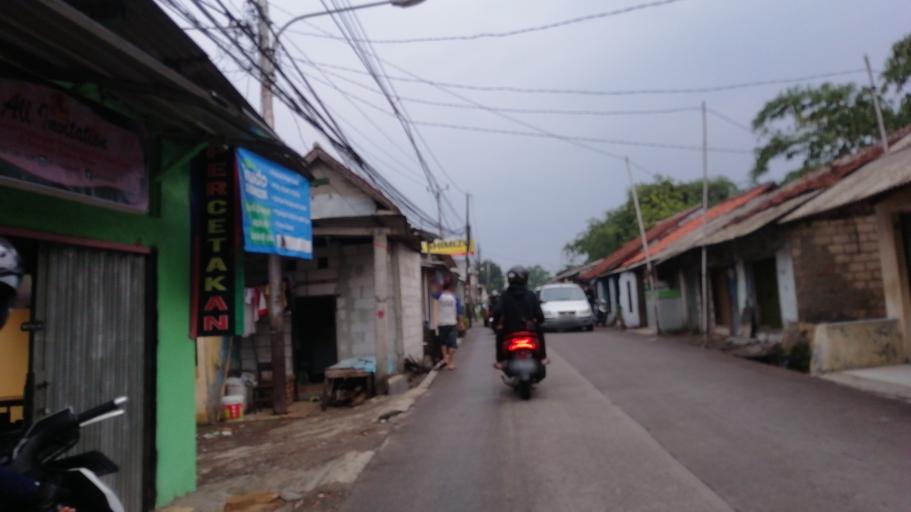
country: ID
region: West Java
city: Bogor
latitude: -6.5339
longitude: 106.7997
